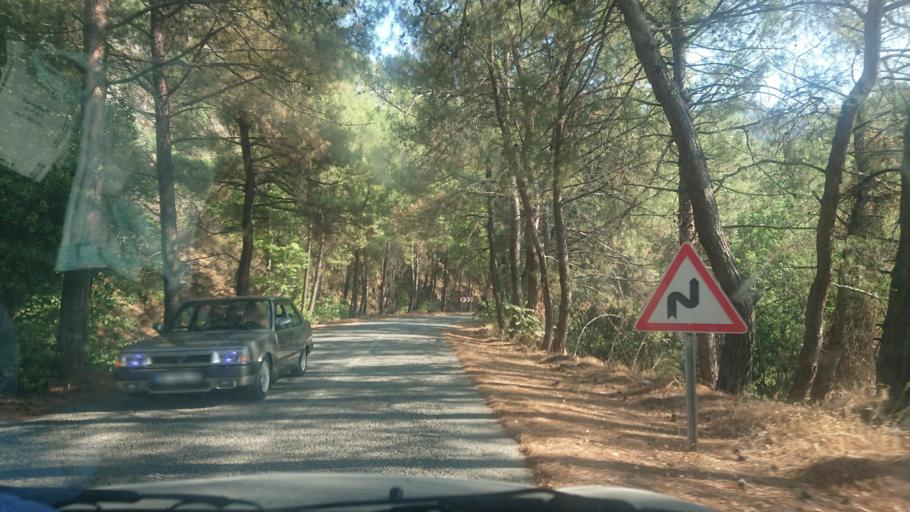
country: TR
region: Aydin
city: Atburgazi
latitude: 37.6917
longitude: 27.1531
